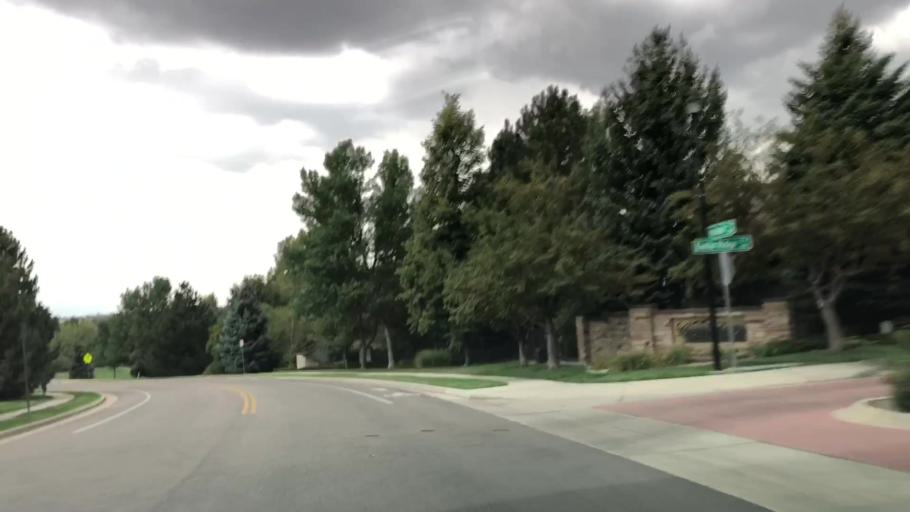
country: US
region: Colorado
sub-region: Larimer County
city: Fort Collins
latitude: 40.5144
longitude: -105.0648
